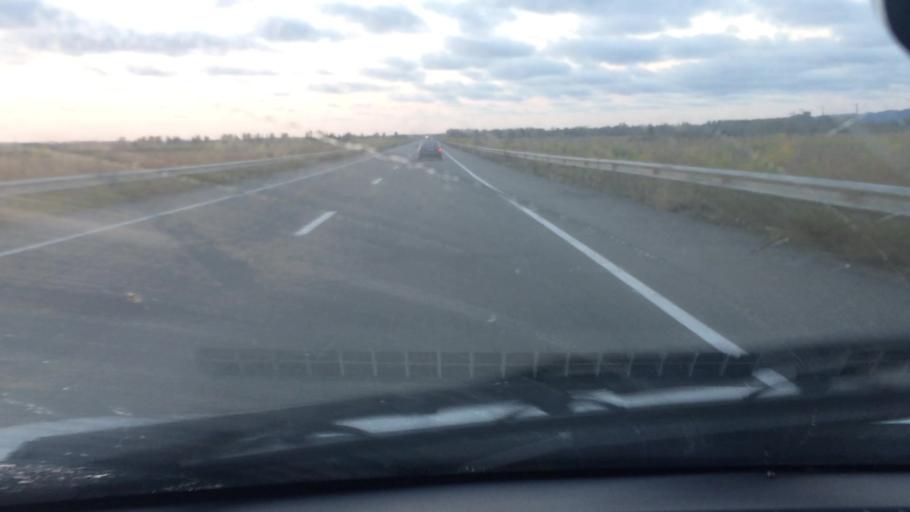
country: GE
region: Ajaria
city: Ochkhamuri
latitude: 41.8744
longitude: 41.8266
